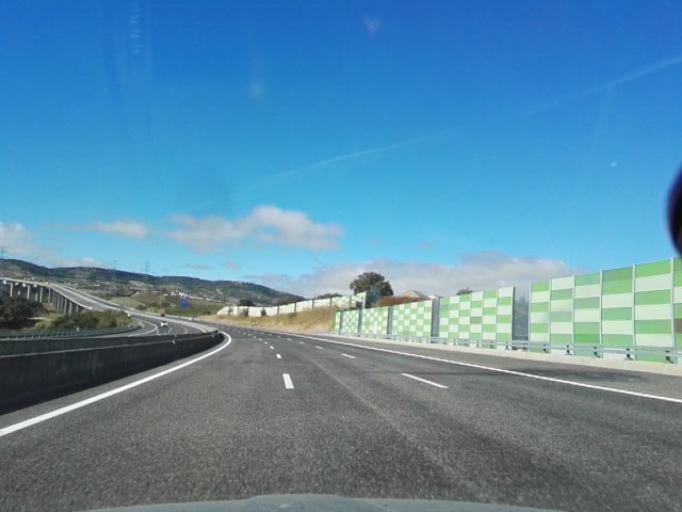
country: PT
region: Lisbon
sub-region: Arruda Dos Vinhos
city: Arruda dos Vinhos
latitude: 38.9873
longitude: -9.0481
